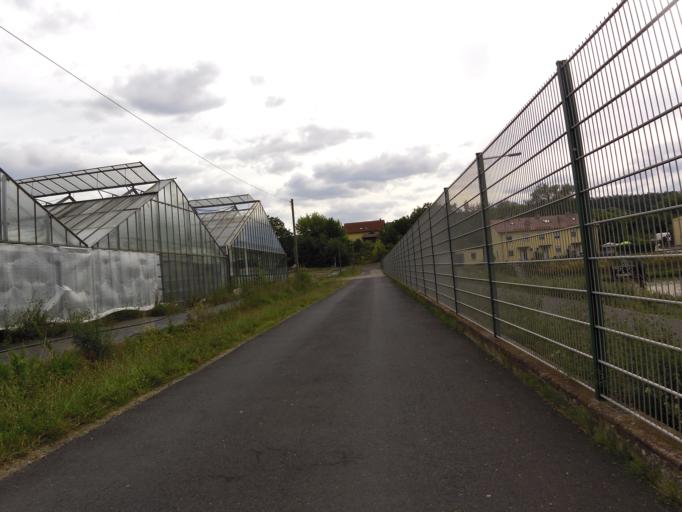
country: DE
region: Bavaria
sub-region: Regierungsbezirk Unterfranken
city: Randersacker
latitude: 49.7516
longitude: 9.9799
